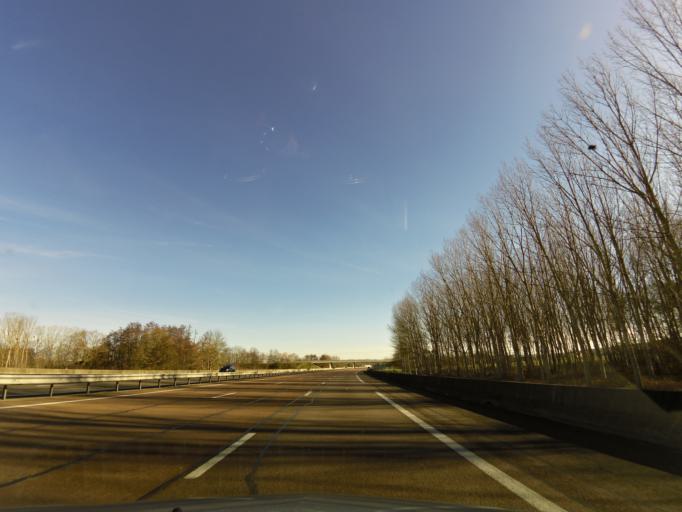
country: FR
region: Bourgogne
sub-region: Departement de l'Yonne
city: Appoigny
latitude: 47.8643
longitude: 3.5253
